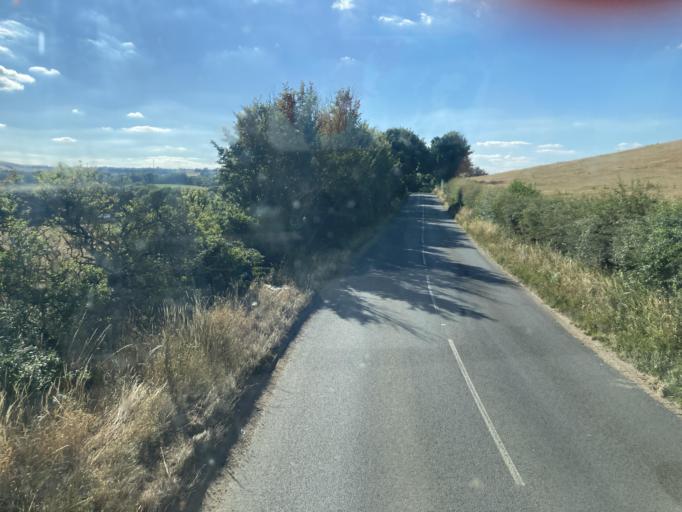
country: GB
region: England
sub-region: Isle of Wight
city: Newport
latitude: 50.6725
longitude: -1.2771
